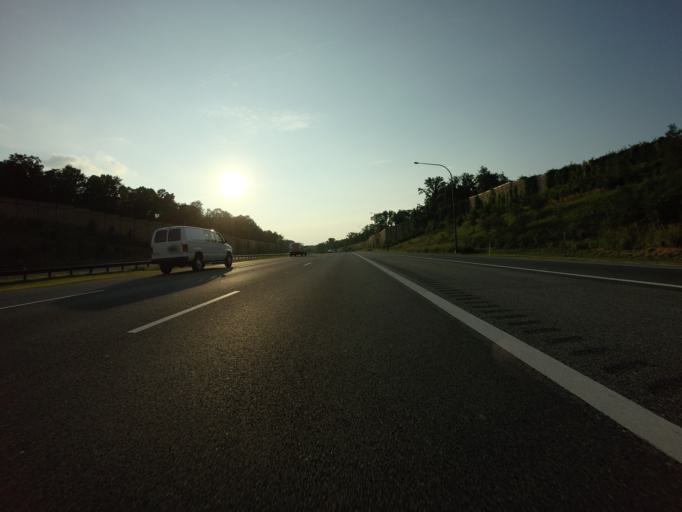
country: US
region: Maryland
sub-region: Montgomery County
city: Fairland
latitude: 39.0813
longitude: -76.9587
